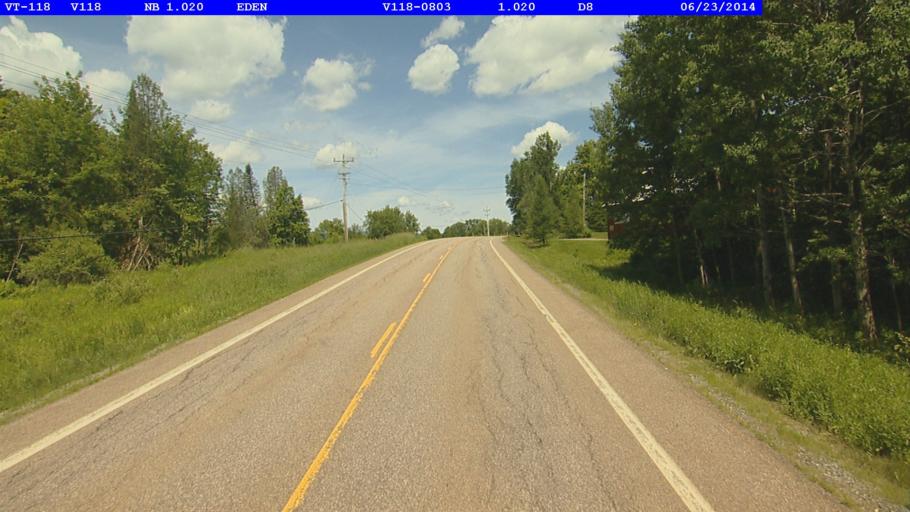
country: US
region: Vermont
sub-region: Lamoille County
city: Hyde Park
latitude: 44.7193
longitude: -72.5580
